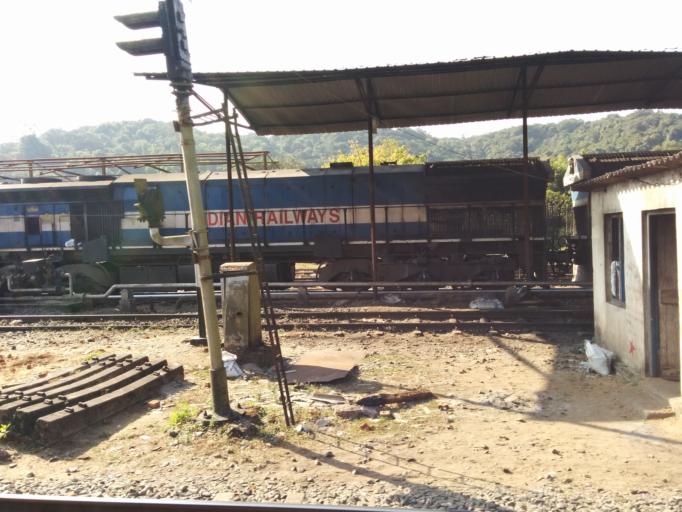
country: IN
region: Karnataka
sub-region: Belgaum
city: Londa
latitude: 15.3990
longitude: 74.3307
